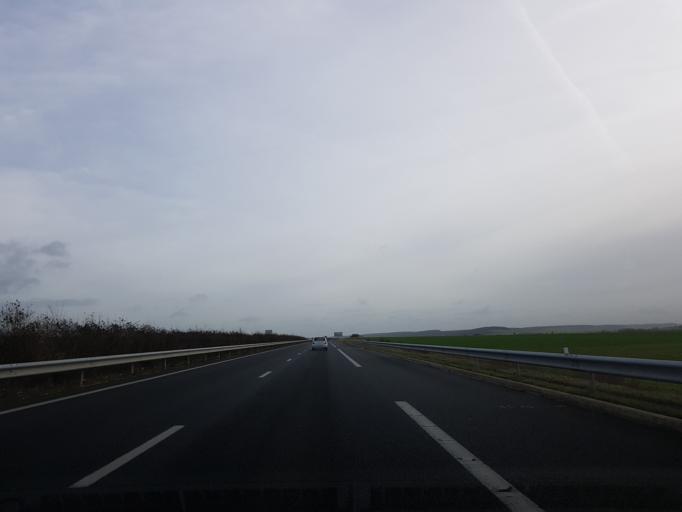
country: FR
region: Champagne-Ardenne
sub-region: Departement de l'Aube
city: Aix-en-Othe
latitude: 48.2429
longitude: 3.5735
